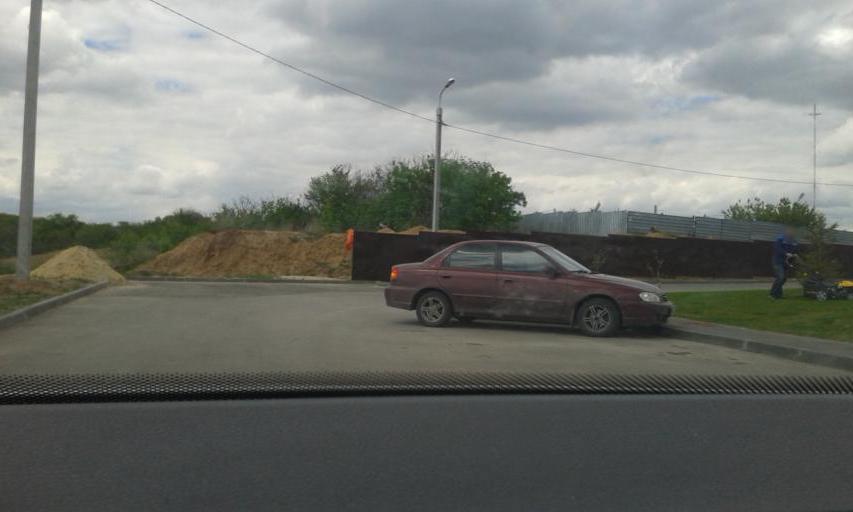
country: RU
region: Volgograd
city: Volgograd
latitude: 48.6628
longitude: 44.4068
